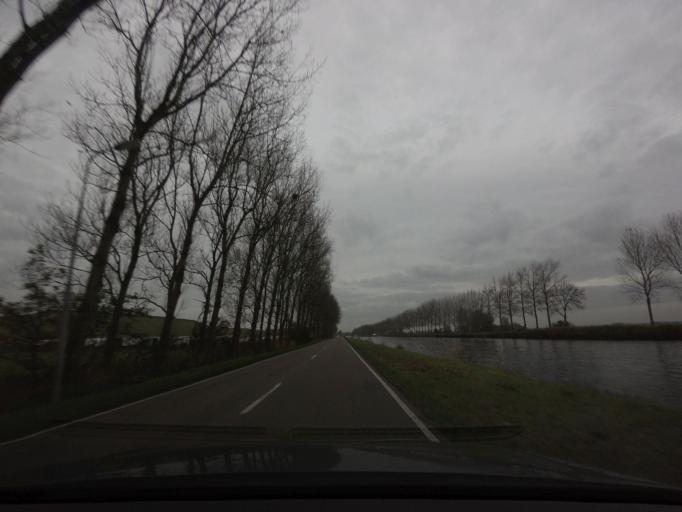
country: NL
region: North Holland
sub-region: Gemeente Alkmaar
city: Alkmaar
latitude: 52.5955
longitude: 4.7582
